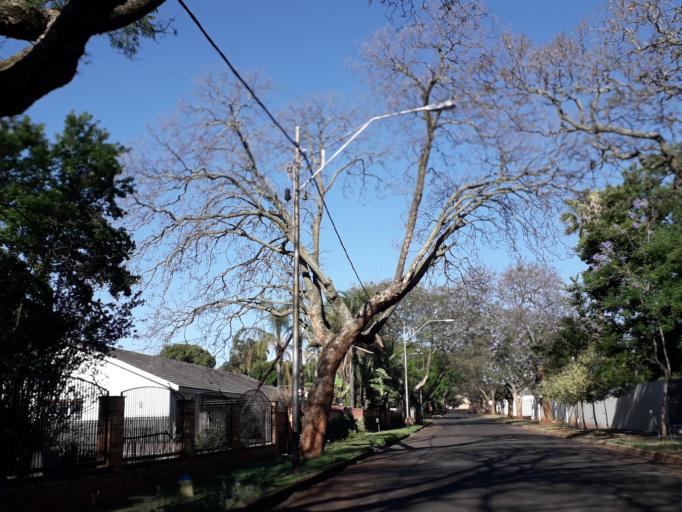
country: ZA
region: Gauteng
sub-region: City of Johannesburg Metropolitan Municipality
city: Johannesburg
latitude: -26.1620
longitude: 28.0080
